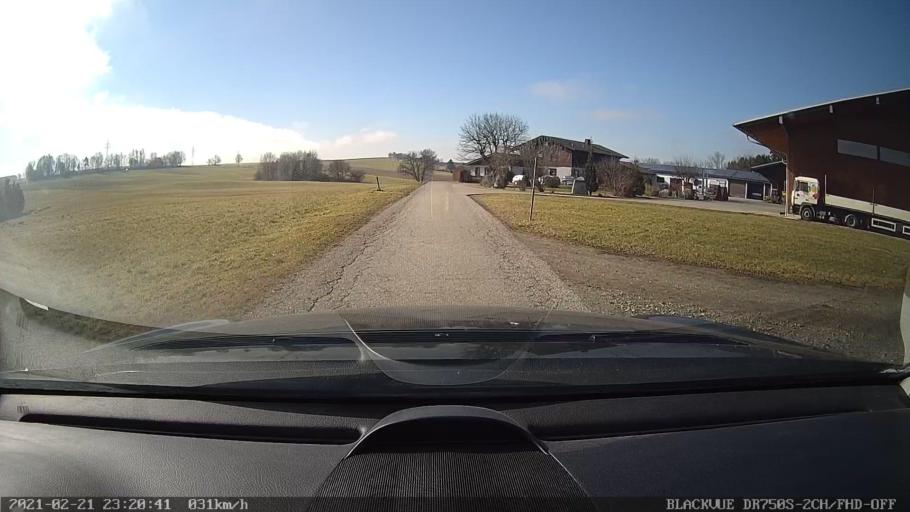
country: DE
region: Bavaria
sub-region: Upper Bavaria
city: Griesstatt
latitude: 48.0039
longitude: 12.1995
